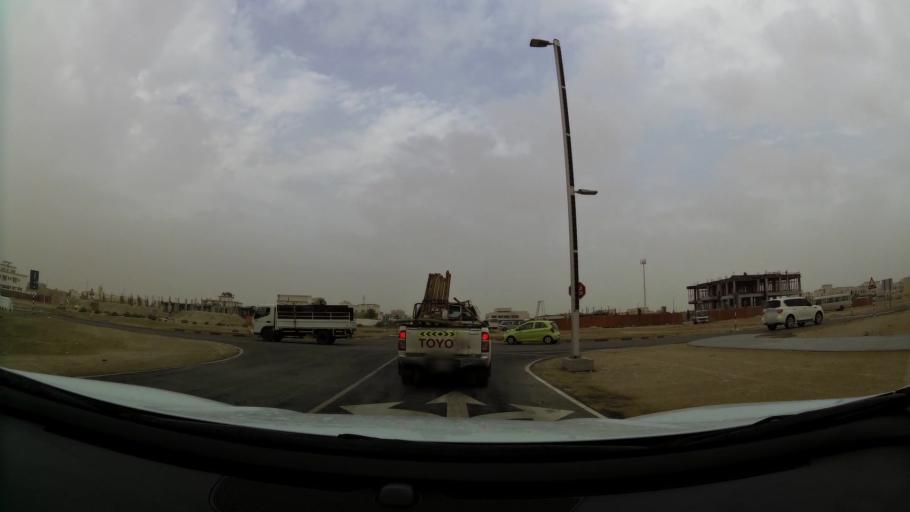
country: AE
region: Abu Dhabi
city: Abu Dhabi
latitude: 24.4176
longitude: 54.6094
